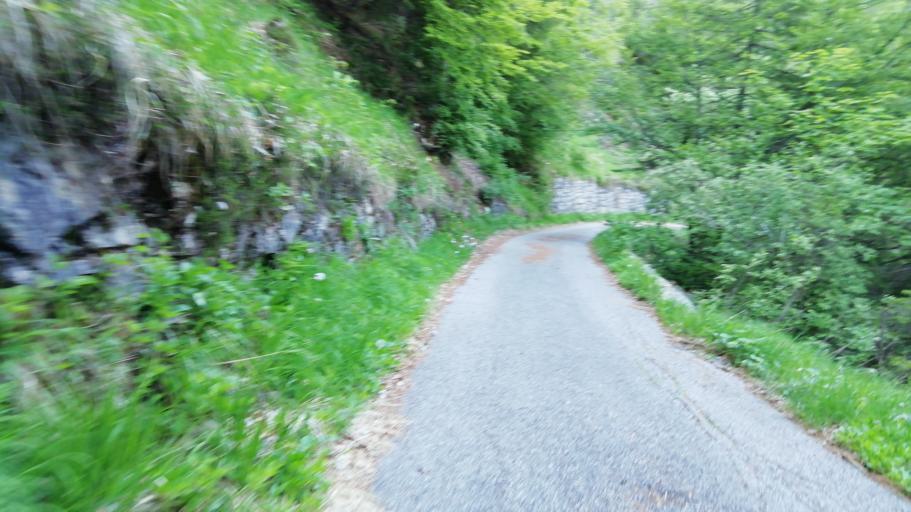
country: IT
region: Veneto
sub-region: Provincia di Belluno
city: Valle di Cadore
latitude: 46.4271
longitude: 12.3224
